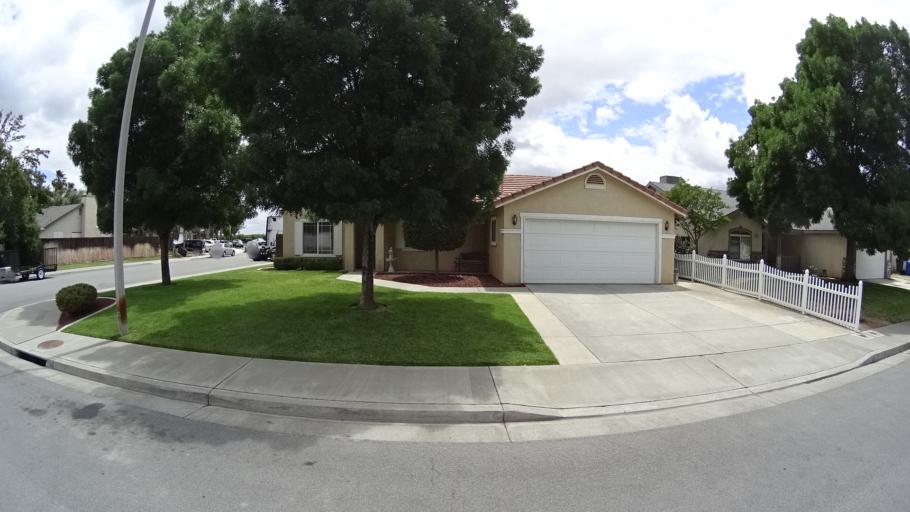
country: US
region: California
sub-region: Kings County
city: Hanford
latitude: 36.3369
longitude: -119.6250
